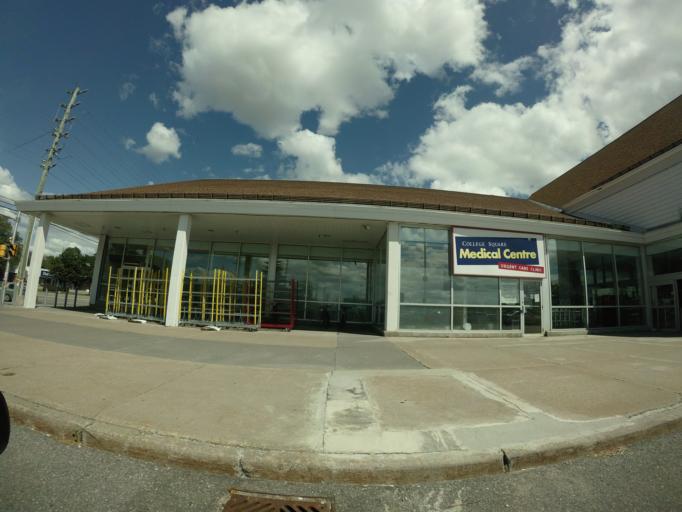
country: CA
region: Ontario
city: Bells Corners
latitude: 45.3522
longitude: -75.7603
